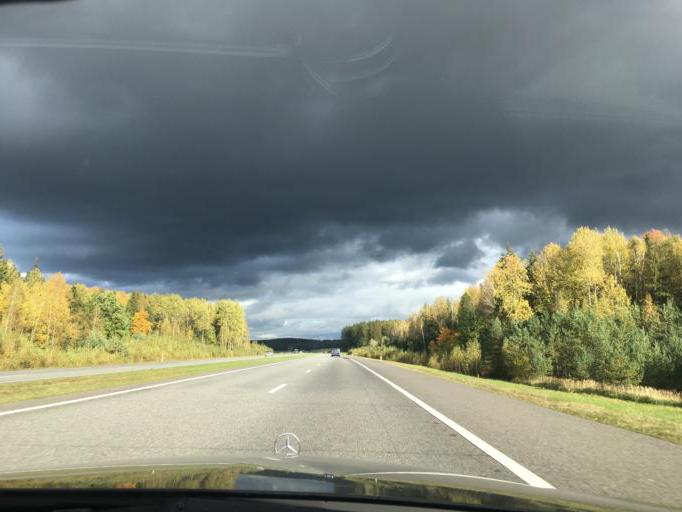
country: BY
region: Vitebsk
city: Talachyn
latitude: 54.4070
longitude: 29.4882
